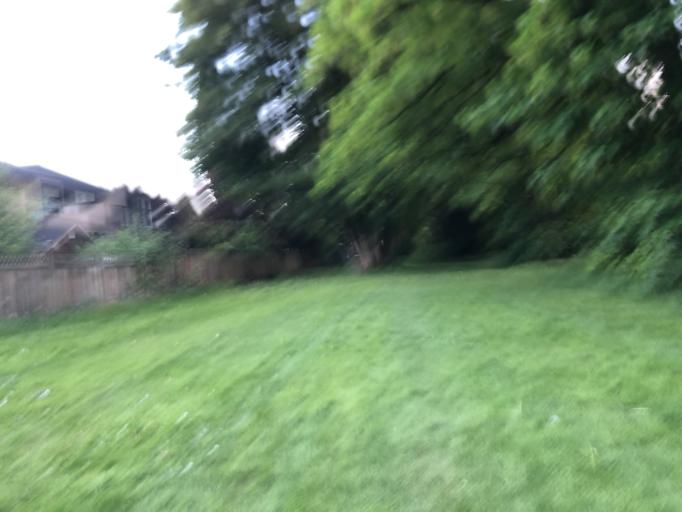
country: CA
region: British Columbia
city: Richmond
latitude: 49.1347
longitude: -123.1253
